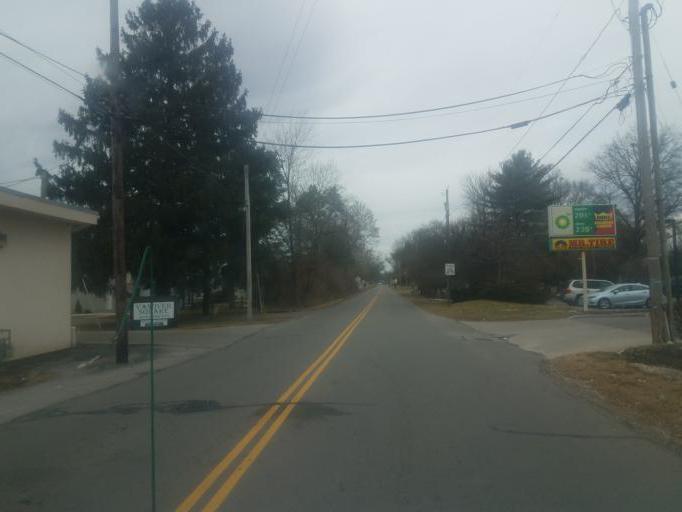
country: US
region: Ohio
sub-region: Marion County
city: Marion
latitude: 40.5810
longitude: -83.1024
